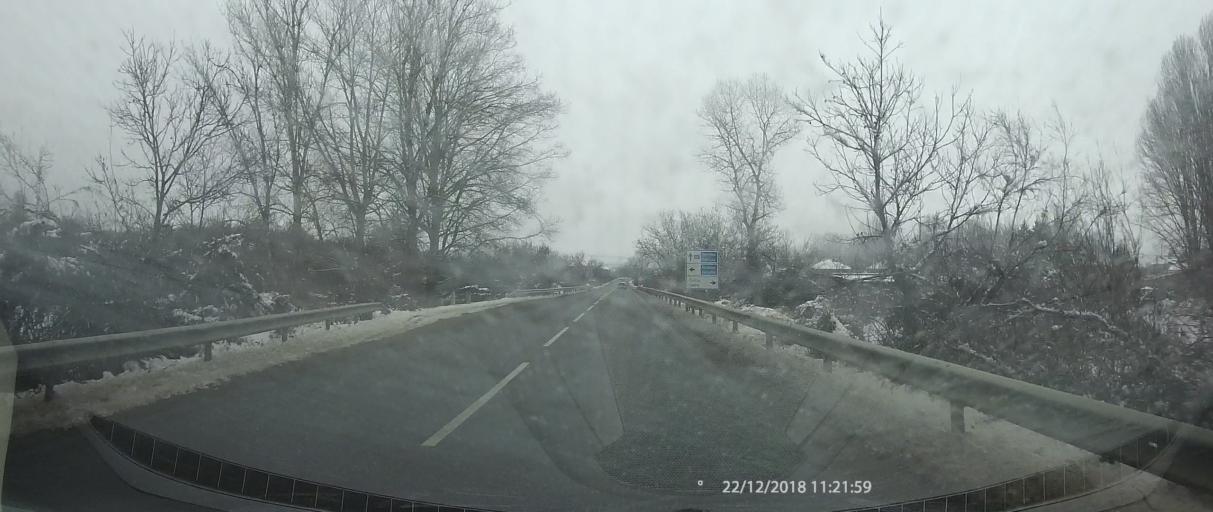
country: BG
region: Kyustendil
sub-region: Obshtina Kyustendil
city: Kyustendil
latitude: 42.2576
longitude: 22.8512
